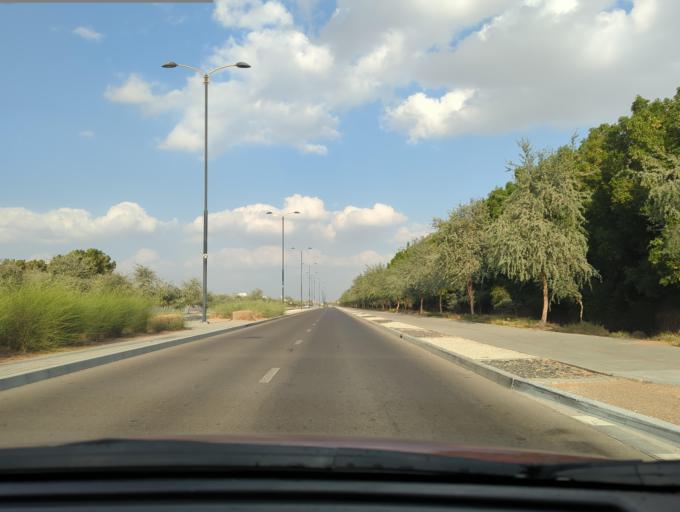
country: AE
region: Abu Dhabi
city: Al Ain
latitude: 24.1547
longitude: 55.6617
